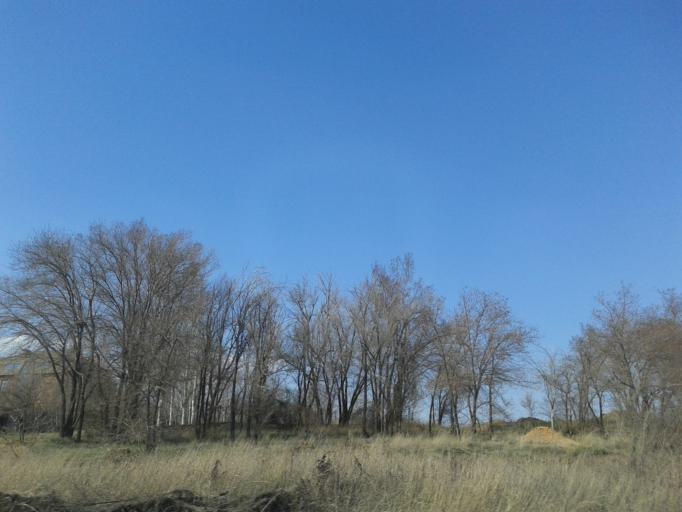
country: RU
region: Volgograd
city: Volgograd
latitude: 48.6304
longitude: 44.4033
